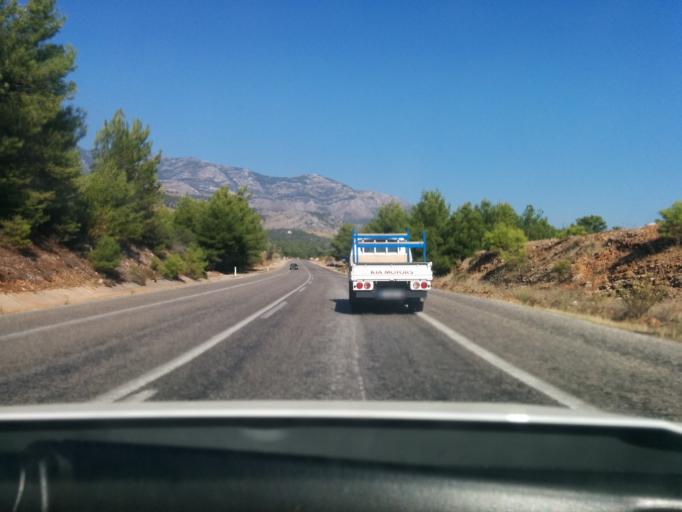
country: TR
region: Mugla
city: Esen
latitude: 36.4283
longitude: 29.2725
